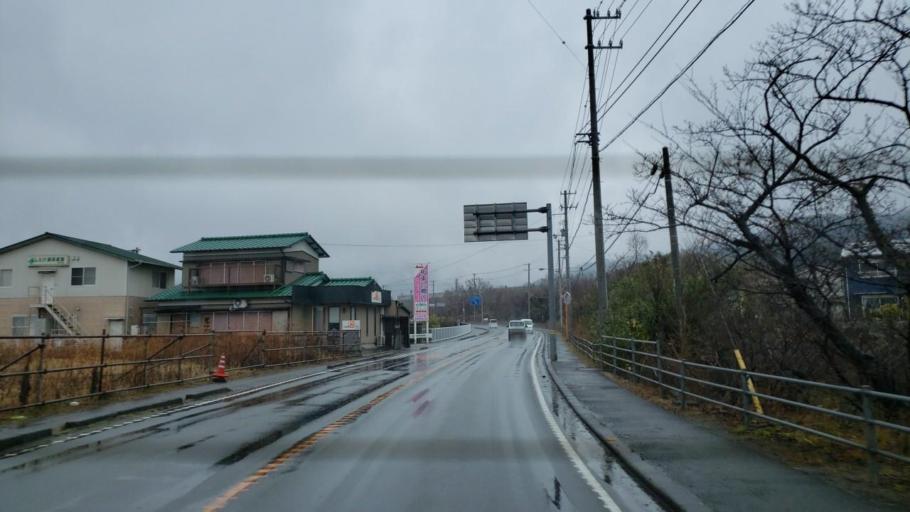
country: JP
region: Tokushima
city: Tokushima-shi
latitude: 34.1568
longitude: 134.5093
